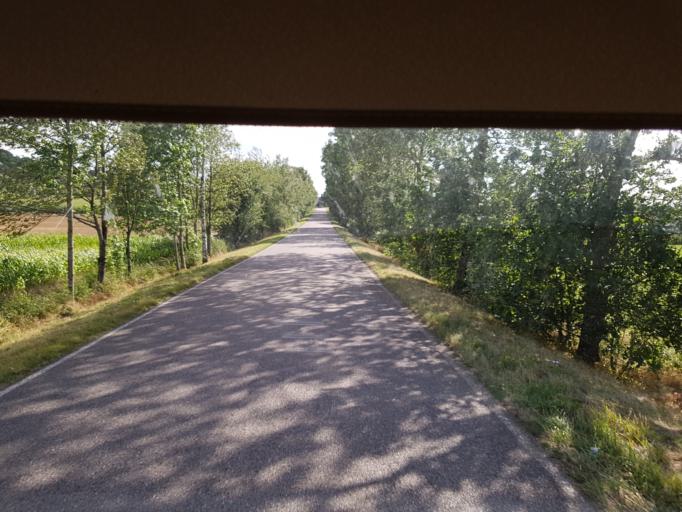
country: LU
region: Grevenmacher
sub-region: Canton de Remich
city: Remich
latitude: 49.5235
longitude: 6.4253
